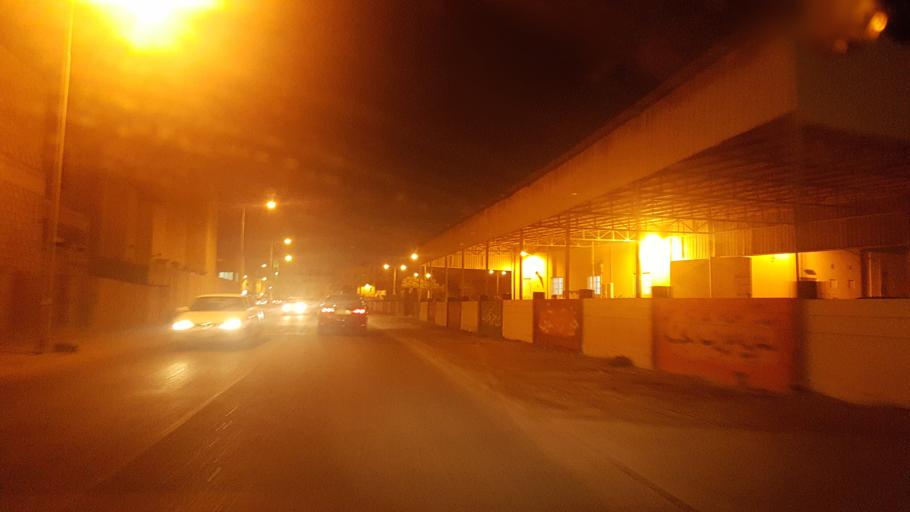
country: BH
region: Manama
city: Jidd Hafs
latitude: 26.2277
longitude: 50.5150
